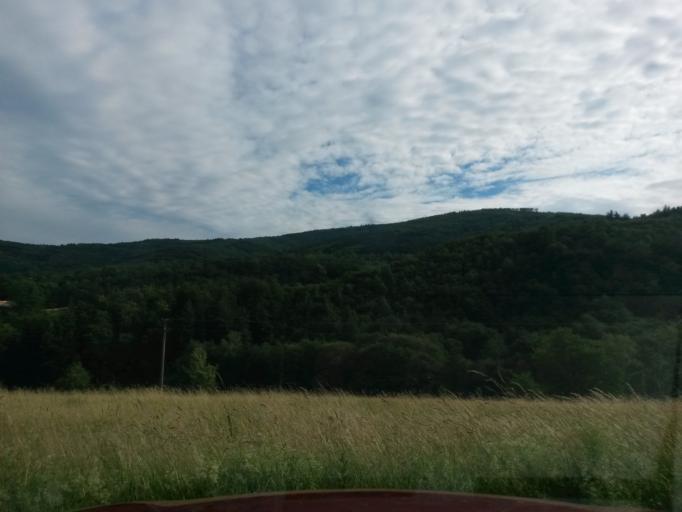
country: SK
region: Banskobystricky
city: Detva
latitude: 48.4567
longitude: 19.3141
